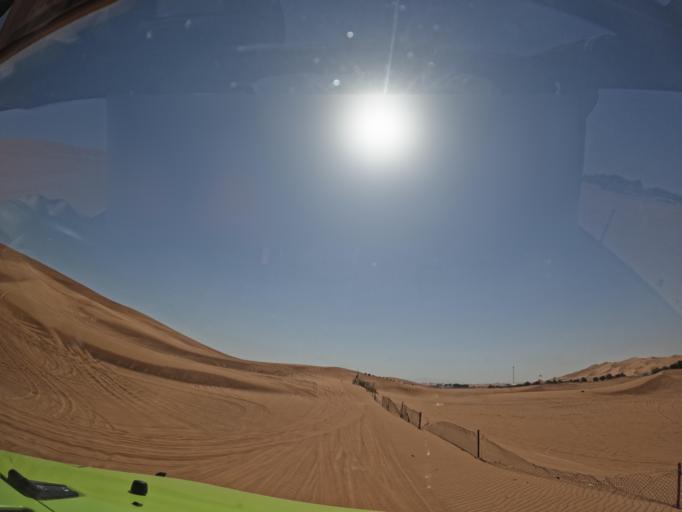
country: AE
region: Ash Shariqah
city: Adh Dhayd
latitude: 24.9589
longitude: 55.7167
